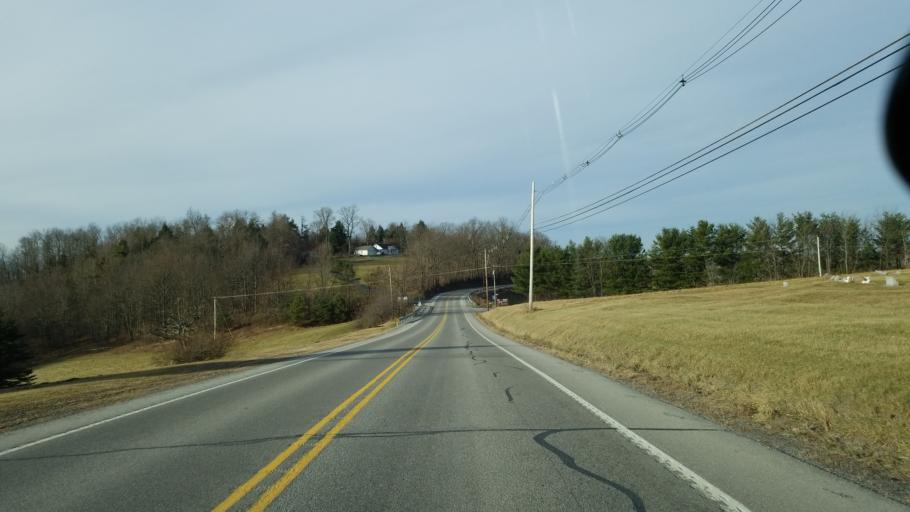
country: US
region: Pennsylvania
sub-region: Clearfield County
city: Curwensville
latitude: 40.9920
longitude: -78.6284
